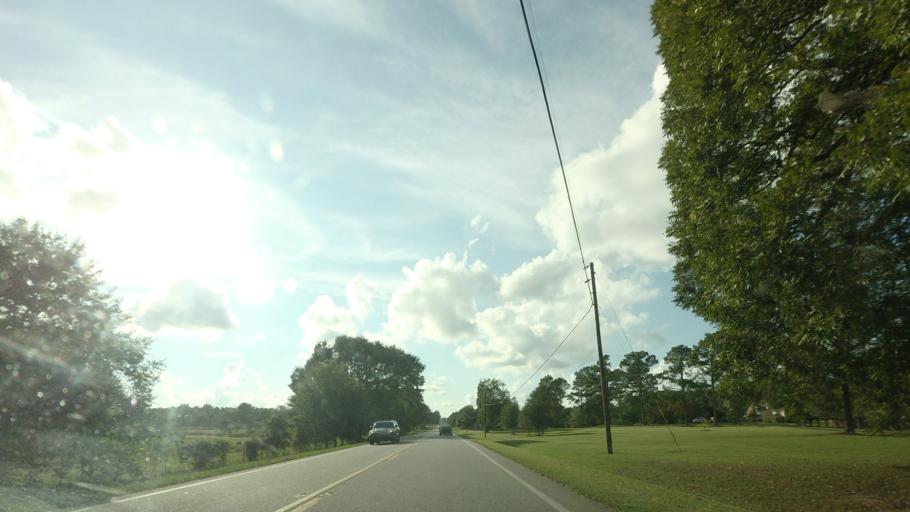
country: US
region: Georgia
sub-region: Pulaski County
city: Hawkinsville
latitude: 32.2875
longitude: -83.4886
